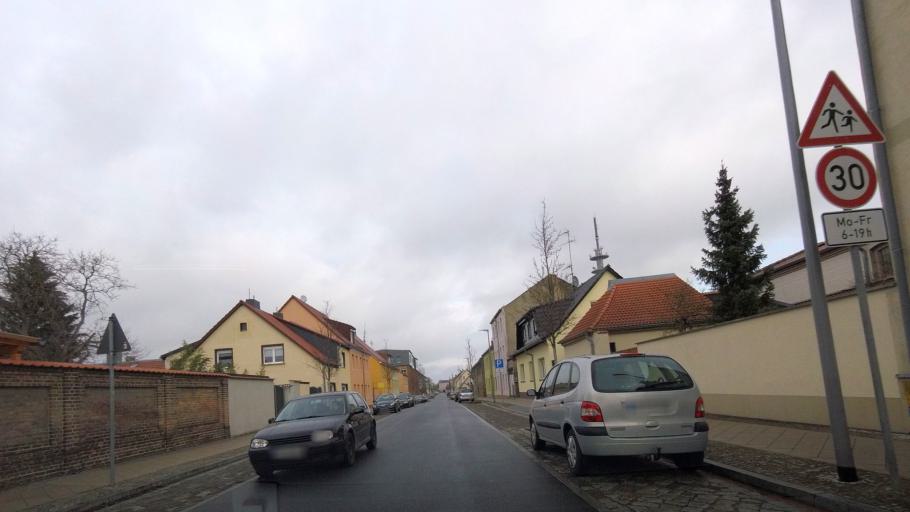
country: DE
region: Brandenburg
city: Luckenwalde
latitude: 52.0909
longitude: 13.1583
